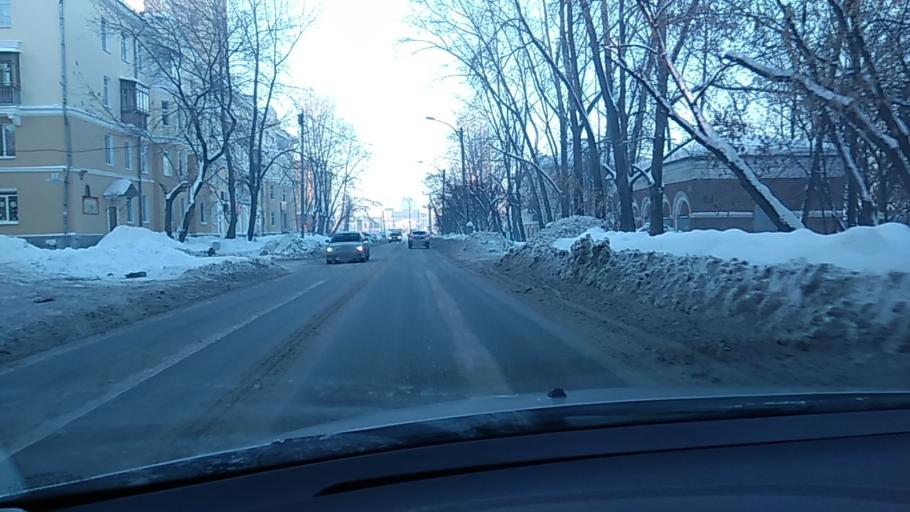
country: RU
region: Sverdlovsk
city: Yekaterinburg
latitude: 56.8623
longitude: 60.6179
